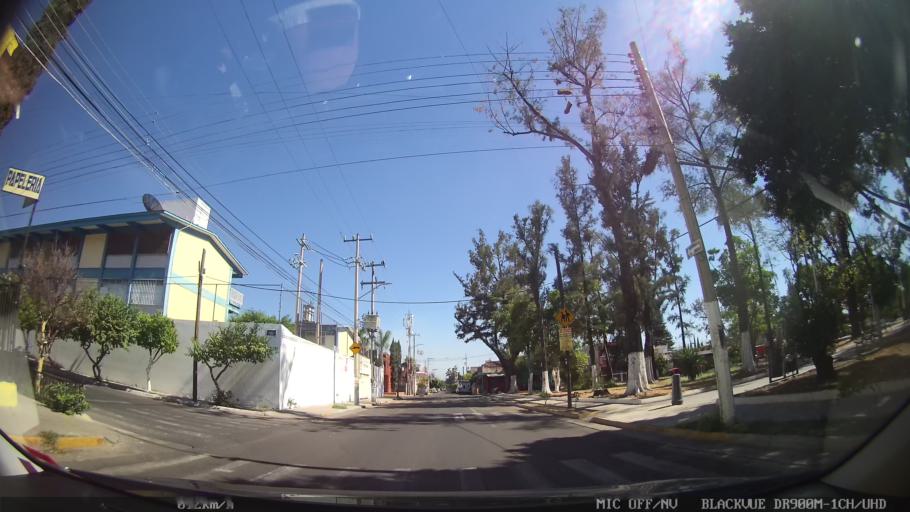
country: MX
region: Jalisco
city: Tlaquepaque
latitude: 20.6606
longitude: -103.2897
